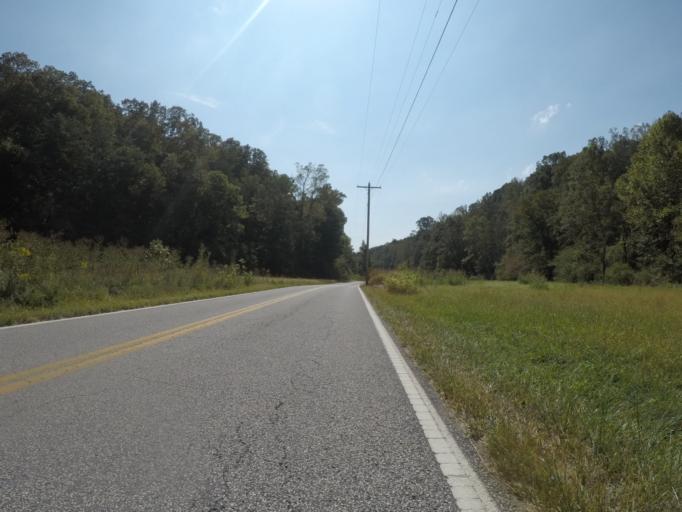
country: US
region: West Virginia
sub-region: Cabell County
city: Lesage
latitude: 38.5722
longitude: -82.4035
